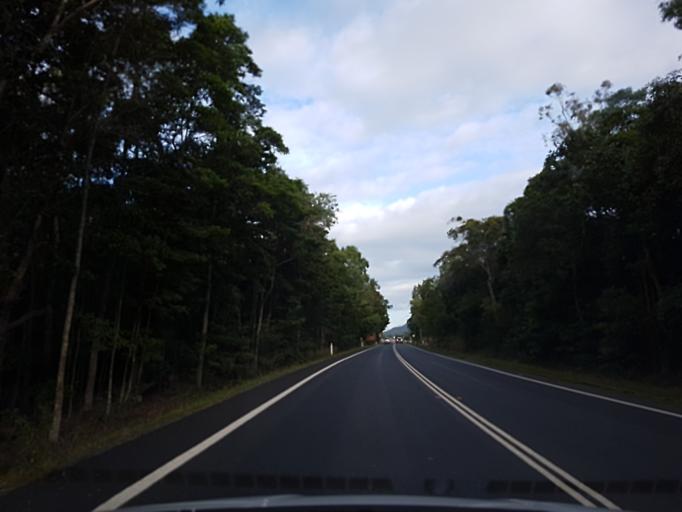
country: AU
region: Queensland
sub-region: Cairns
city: Port Douglas
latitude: -16.5247
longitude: 145.4586
